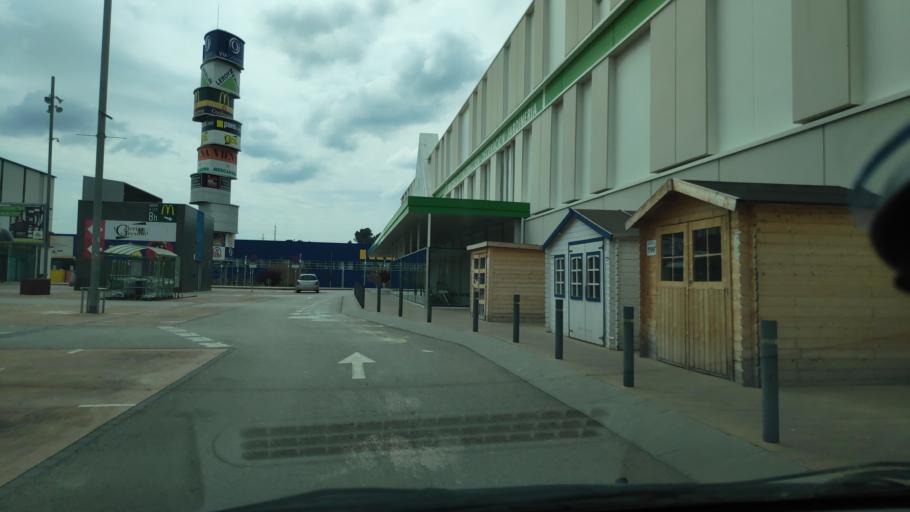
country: ES
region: Catalonia
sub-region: Provincia de Barcelona
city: Barbera del Valles
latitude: 41.5125
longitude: 2.1058
